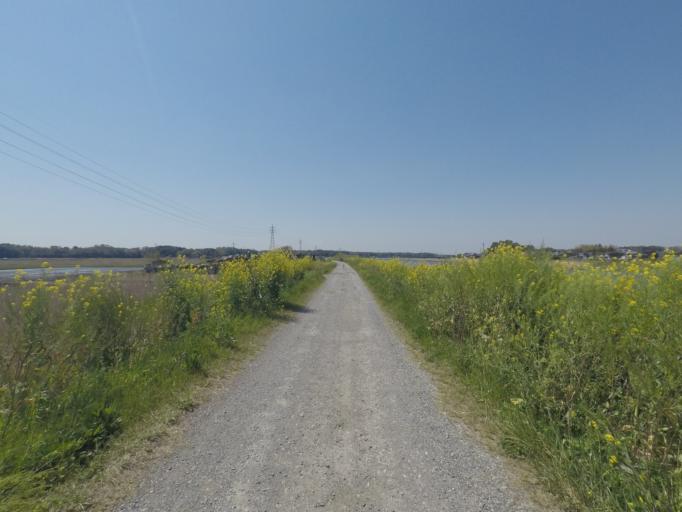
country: JP
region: Ibaraki
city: Ushiku
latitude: 35.9504
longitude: 140.1100
